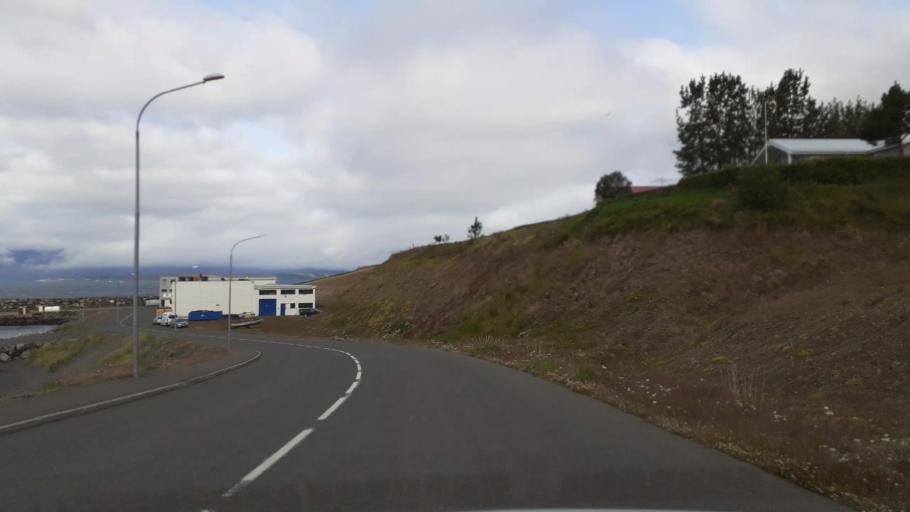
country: IS
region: Northeast
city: Akureyri
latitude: 65.9535
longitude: -18.1809
